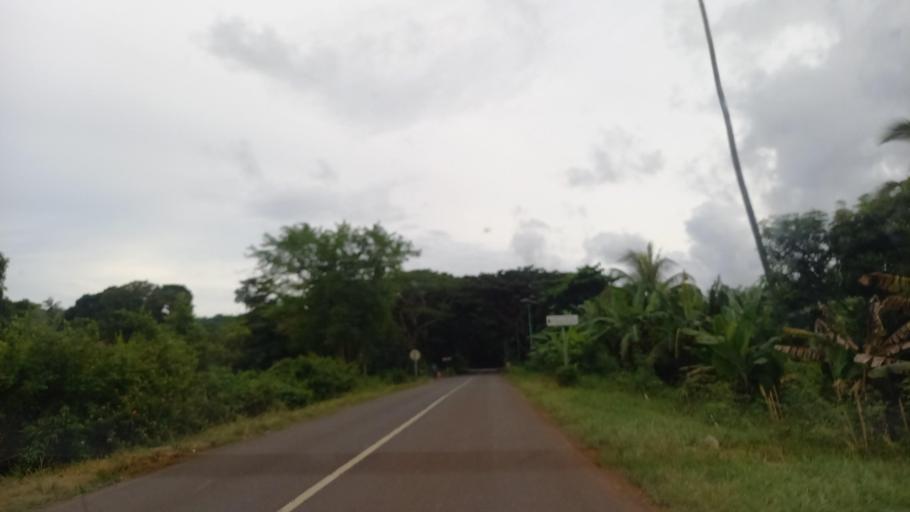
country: YT
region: Chirongui
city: Chirongui
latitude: -12.9154
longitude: 45.1590
